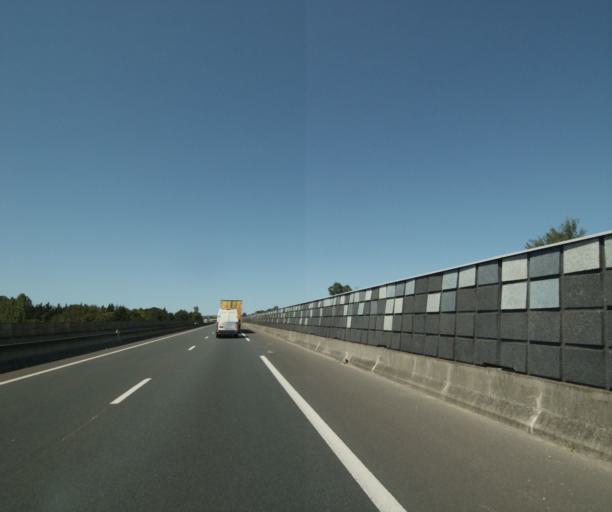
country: FR
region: Midi-Pyrenees
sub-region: Departement du Tarn-et-Garonne
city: Montauban
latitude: 44.0244
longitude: 1.3876
